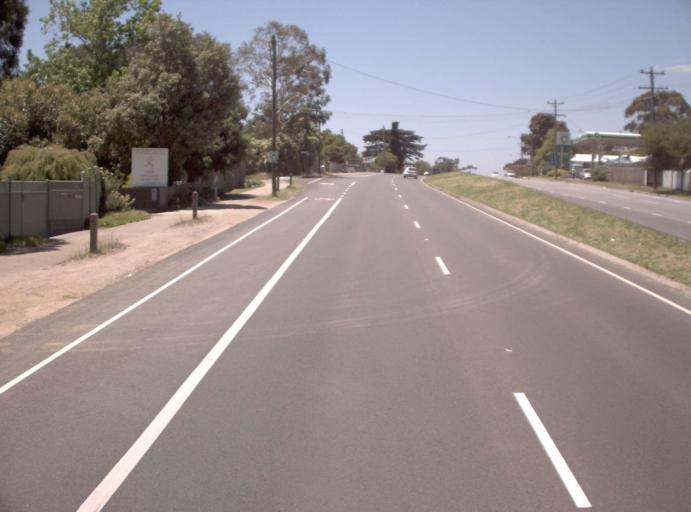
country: AU
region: Victoria
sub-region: Mornington Peninsula
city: Mount Eliza
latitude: -38.2008
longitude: 145.0815
